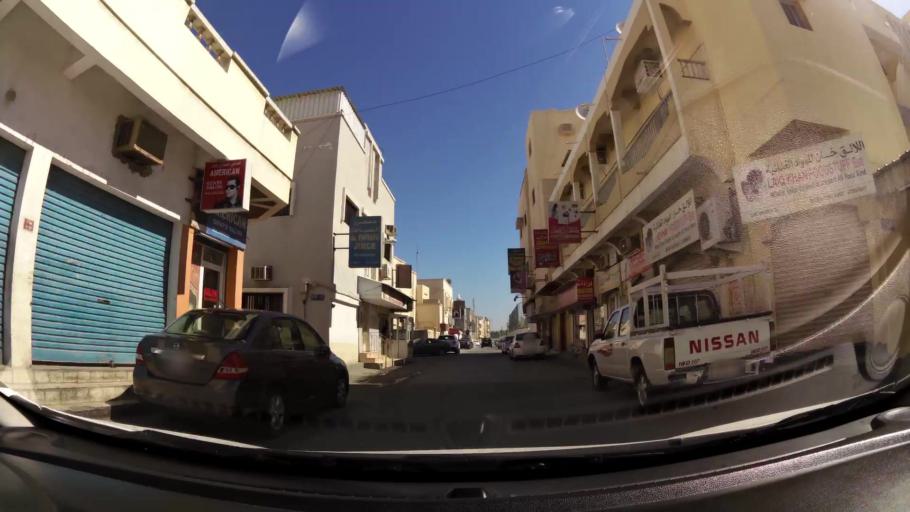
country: BH
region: Muharraq
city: Al Muharraq
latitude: 26.2448
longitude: 50.6158
